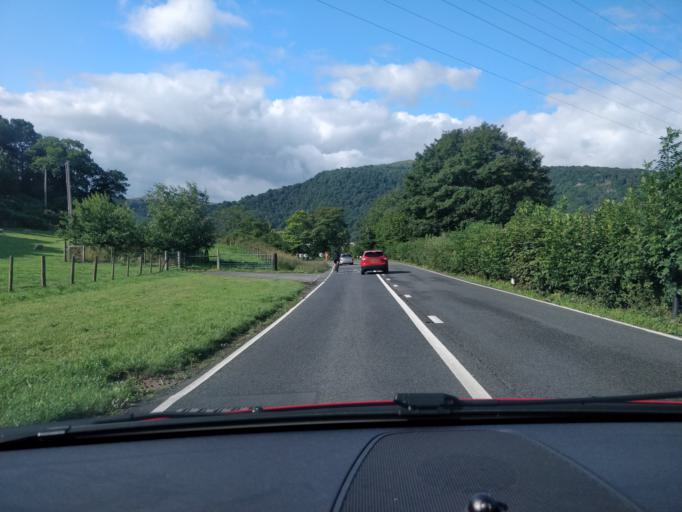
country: GB
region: Wales
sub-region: Conwy
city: Llanrwst
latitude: 53.1955
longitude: -3.8261
